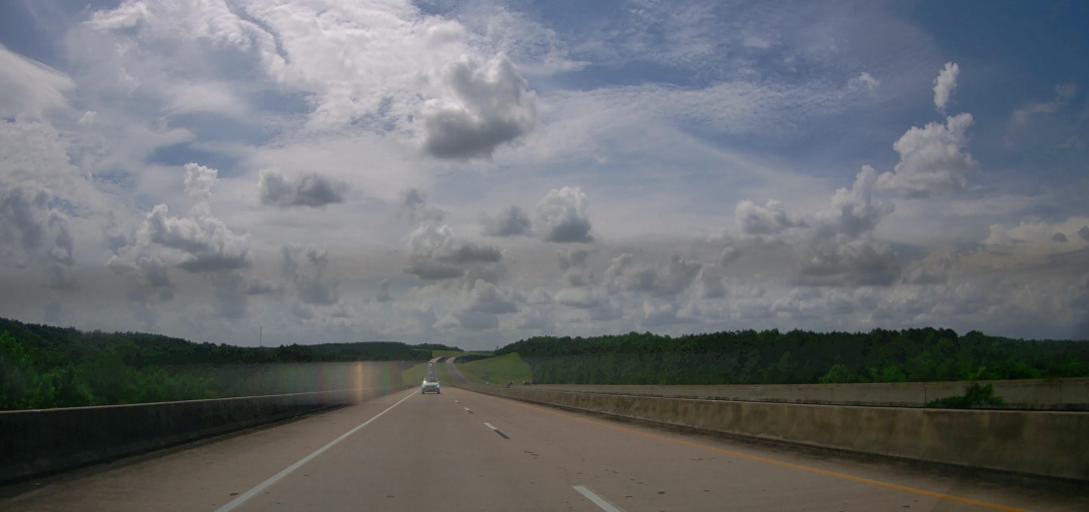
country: US
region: Alabama
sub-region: Marion County
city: Winfield
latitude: 33.9731
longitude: -87.7310
